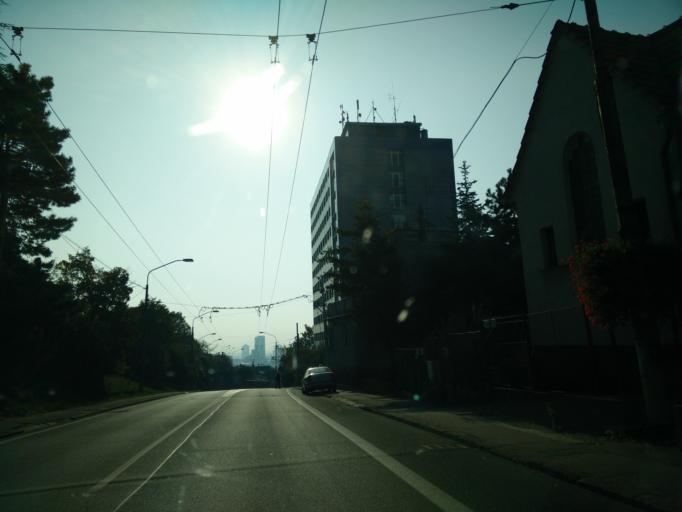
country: SK
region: Bratislavsky
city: Bratislava
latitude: 48.1645
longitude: 17.0968
